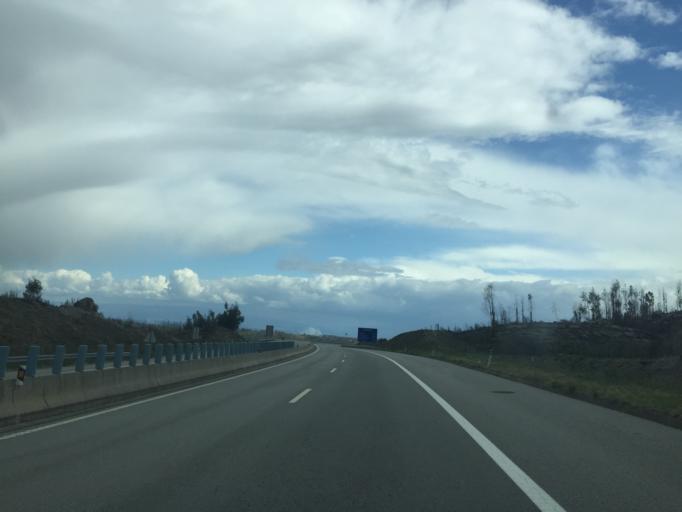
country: PT
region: Viseu
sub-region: Vouzela
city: Vouzela
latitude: 40.6863
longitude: -8.0781
